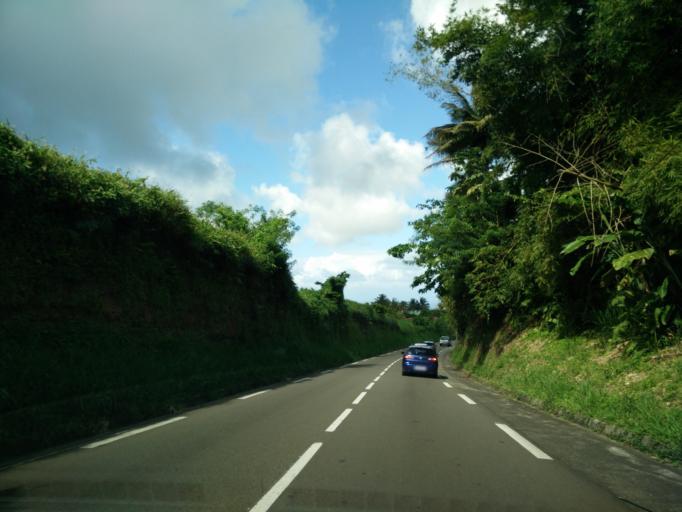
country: MQ
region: Martinique
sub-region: Martinique
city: Le Morne-Rouge
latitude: 14.8038
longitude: -61.1247
